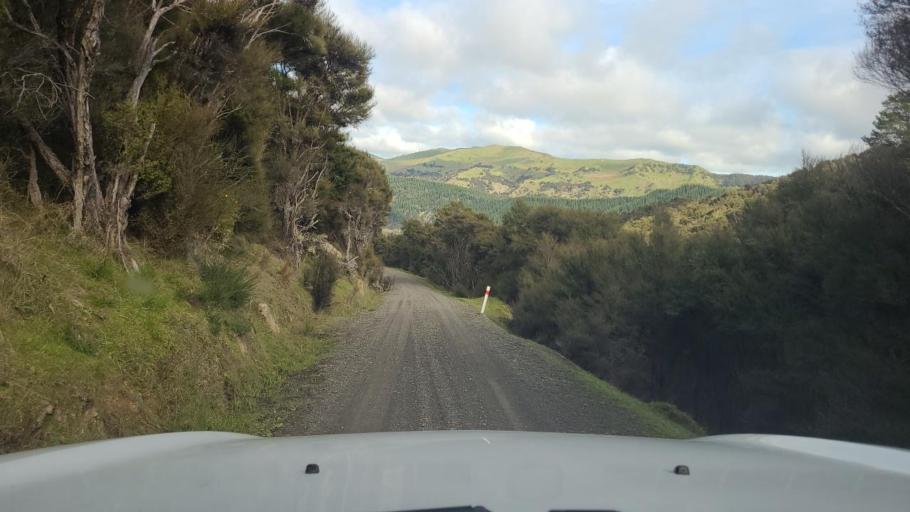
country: NZ
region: Wellington
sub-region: South Wairarapa District
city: Waipawa
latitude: -41.2575
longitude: 175.6904
